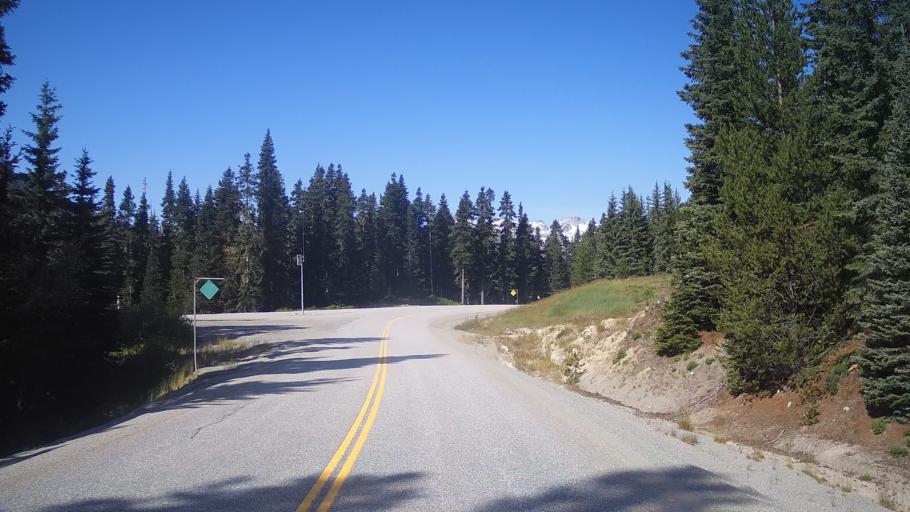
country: CA
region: British Columbia
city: Pemberton
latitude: 50.3811
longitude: -122.4733
